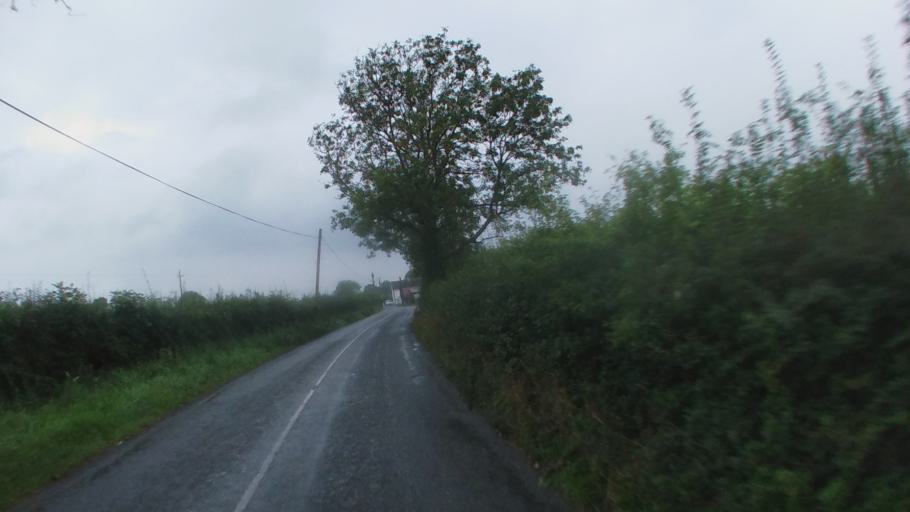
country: IE
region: Leinster
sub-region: Kilkenny
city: Callan
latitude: 52.5115
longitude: -7.4720
